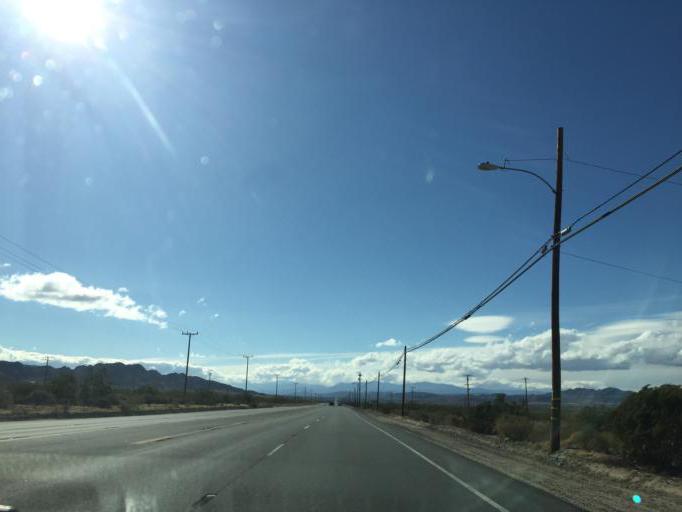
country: US
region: California
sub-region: San Bernardino County
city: Joshua Tree
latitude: 34.1353
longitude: -116.2270
